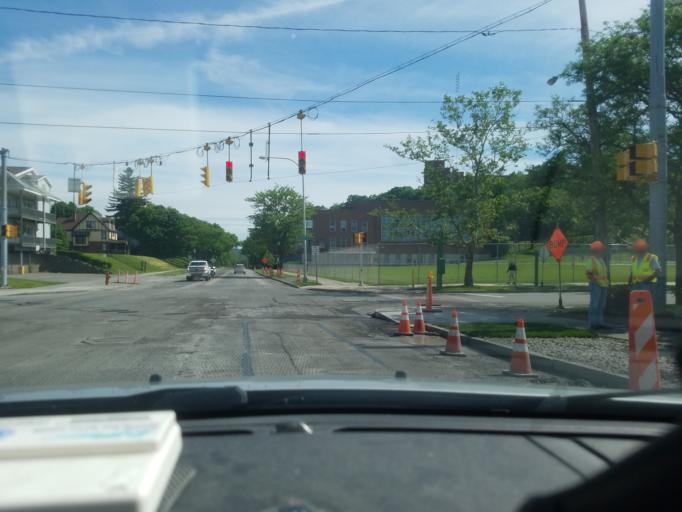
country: US
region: New York
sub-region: Onondaga County
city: Syracuse
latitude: 43.0365
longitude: -76.1299
